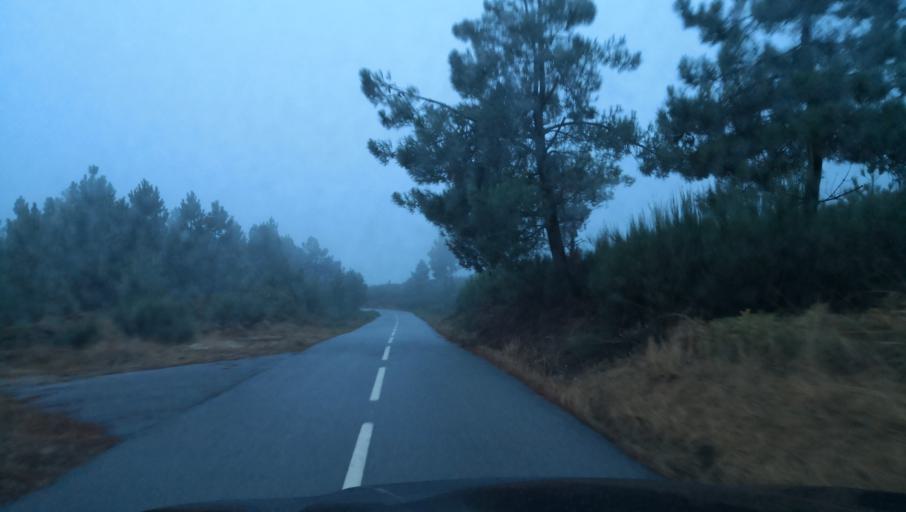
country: PT
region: Vila Real
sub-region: Sabrosa
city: Sabrosa
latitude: 41.2805
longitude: -7.5966
